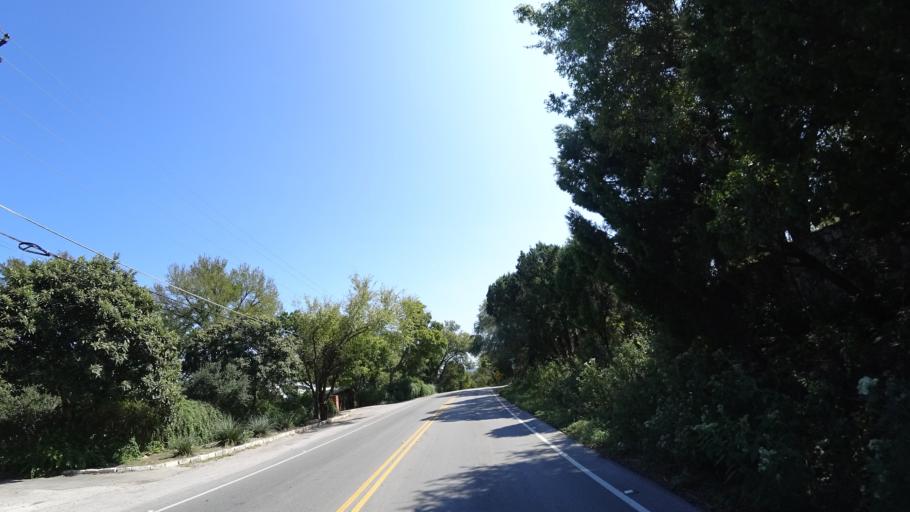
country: US
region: Texas
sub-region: Travis County
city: West Lake Hills
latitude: 30.3004
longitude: -97.7952
